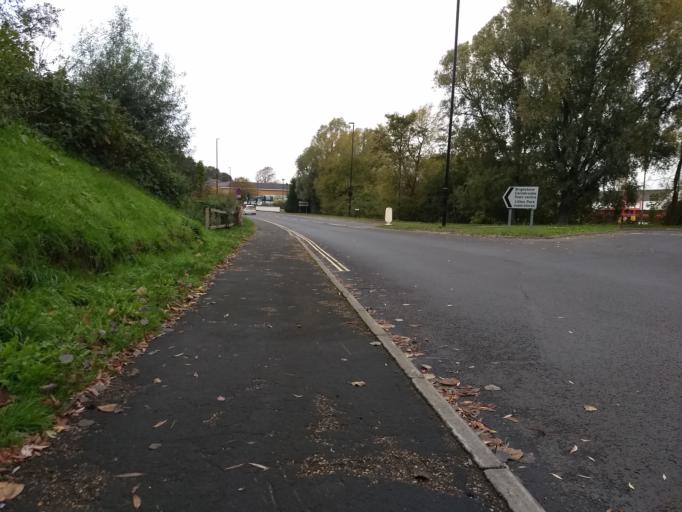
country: GB
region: England
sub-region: Isle of Wight
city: Newport
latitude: 50.6961
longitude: -1.2889
